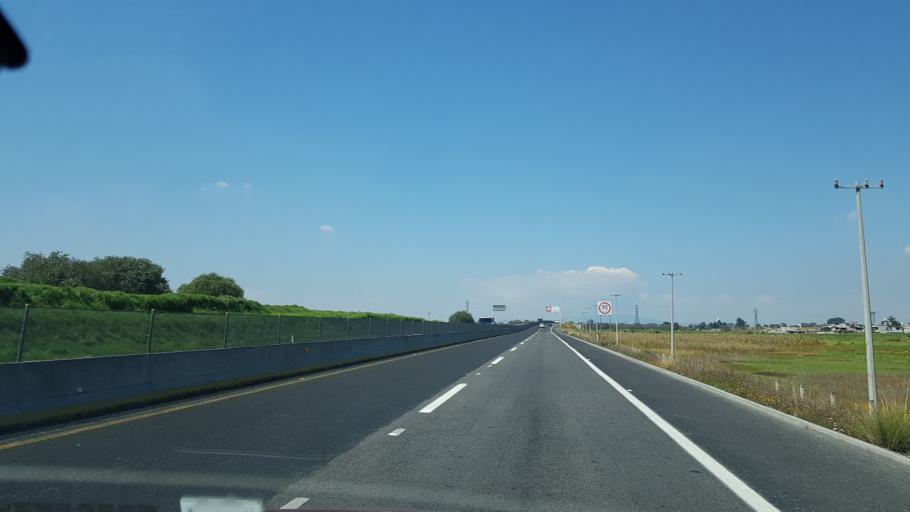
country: MX
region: Mexico
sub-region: Otzolotepec
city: La Y
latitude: 19.4031
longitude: -99.5885
